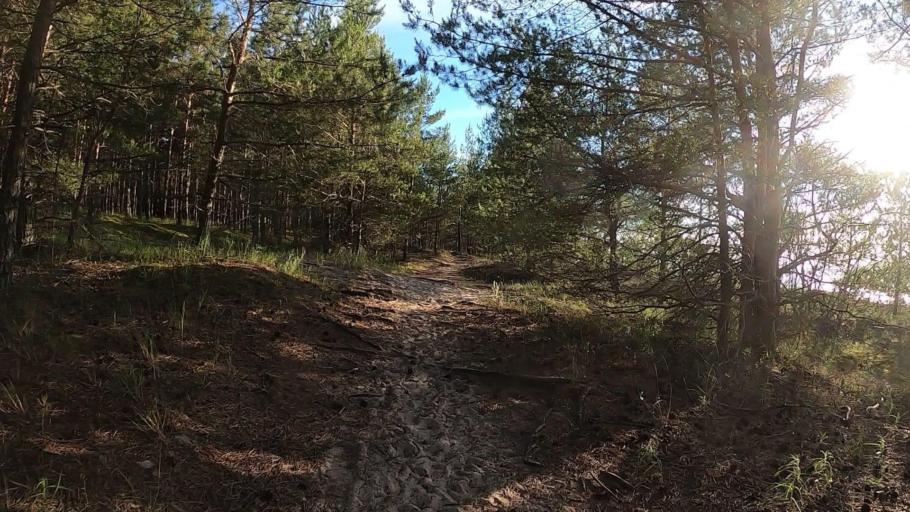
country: LV
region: Riga
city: Jaunciems
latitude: 57.1032
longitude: 24.1670
